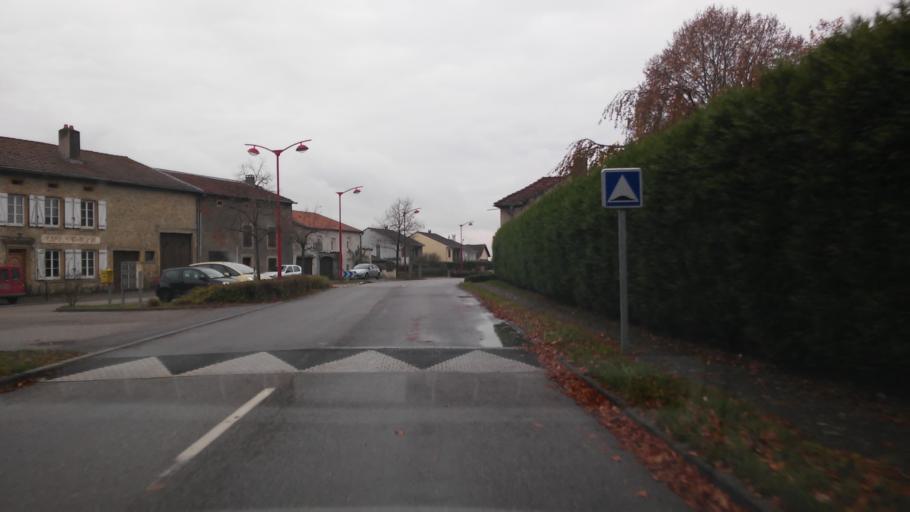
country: FR
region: Lorraine
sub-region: Departement de la Moselle
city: Vigy
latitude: 49.2041
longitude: 6.3632
